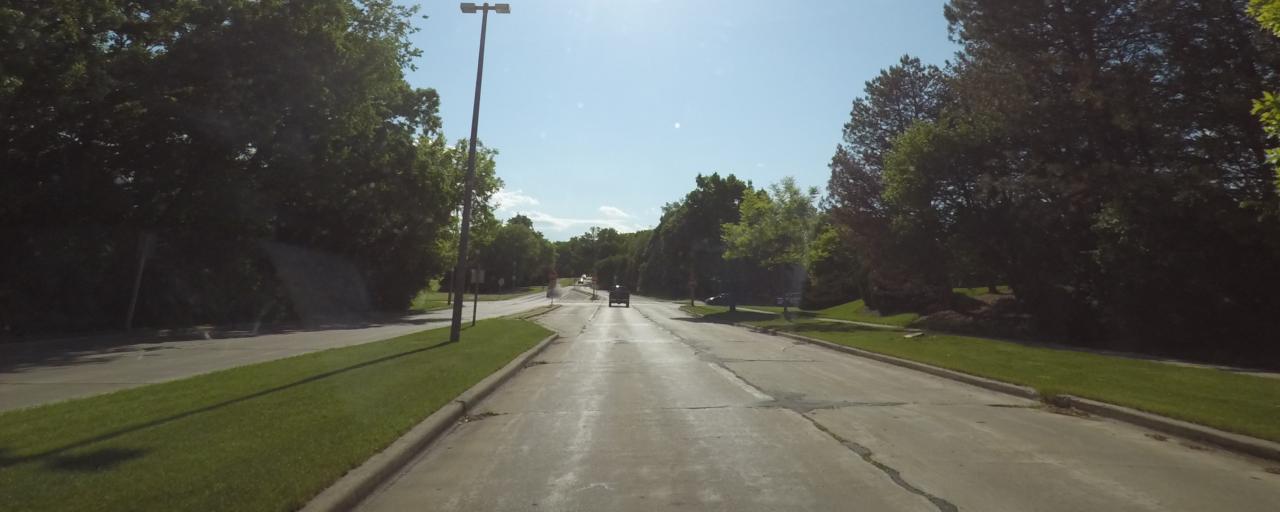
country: US
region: Wisconsin
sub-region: Milwaukee County
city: Greenfield
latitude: 42.9449
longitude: -88.0175
